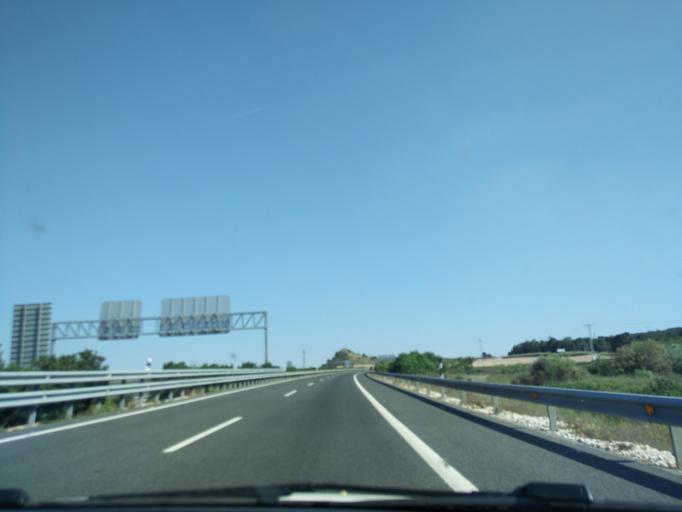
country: ES
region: Murcia
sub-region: Murcia
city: Ojos
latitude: 38.1829
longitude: -1.3194
